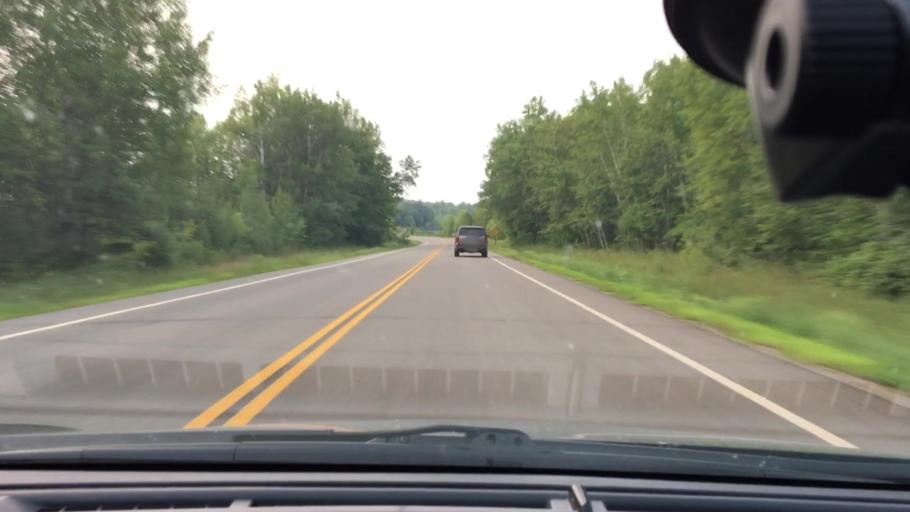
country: US
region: Minnesota
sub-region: Crow Wing County
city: Crosby
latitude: 46.5268
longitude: -93.9266
